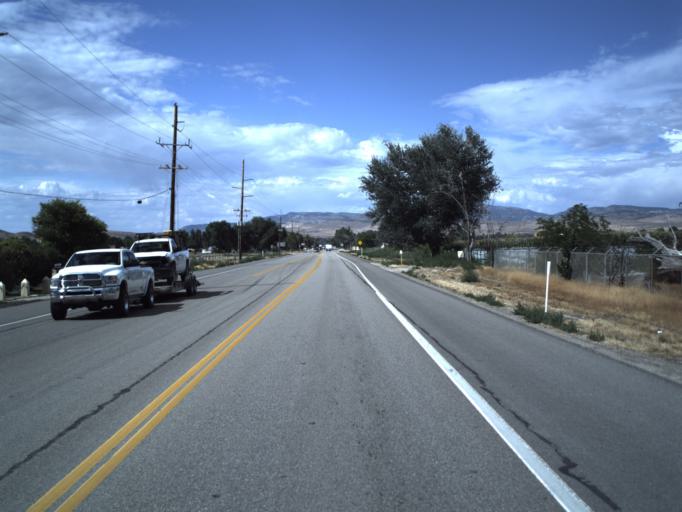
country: US
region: Utah
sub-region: Sanpete County
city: Centerfield
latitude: 39.1127
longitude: -111.8195
